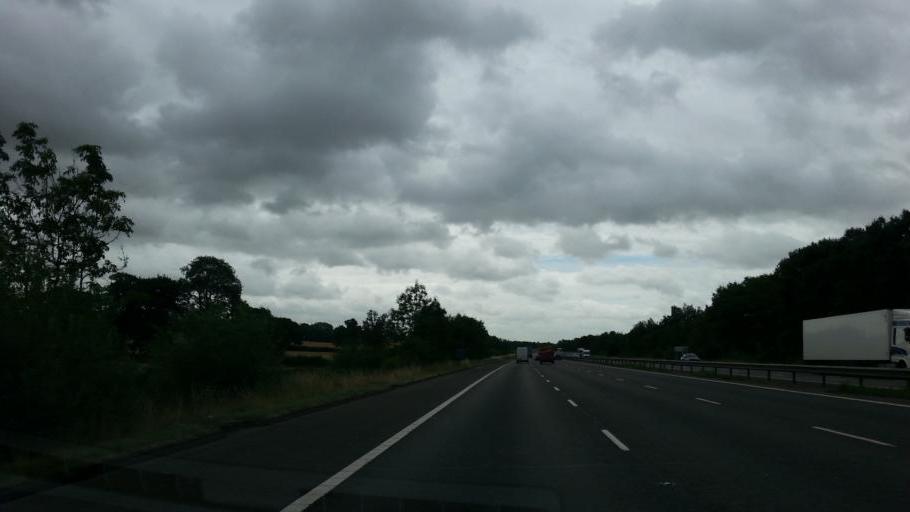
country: GB
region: England
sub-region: Oxfordshire
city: Hanwell
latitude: 52.1058
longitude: -1.3591
